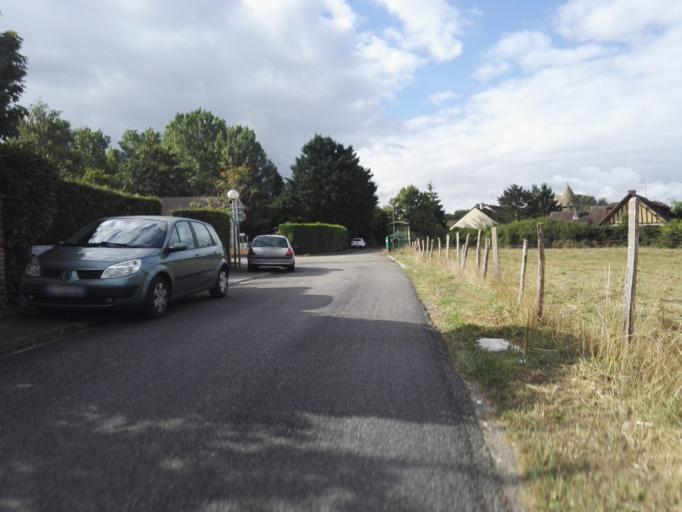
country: FR
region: Haute-Normandie
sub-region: Departement de l'Eure
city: Menilles
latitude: 49.0366
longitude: 1.3567
